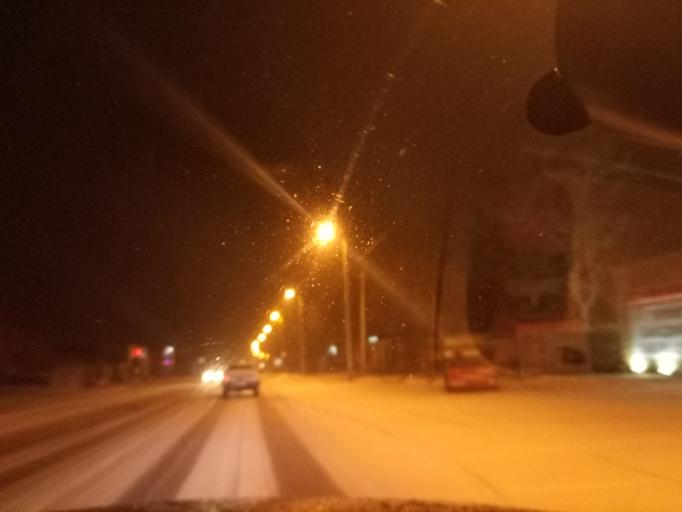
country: RU
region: Tula
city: Novomoskovsk
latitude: 53.9917
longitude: 38.2977
